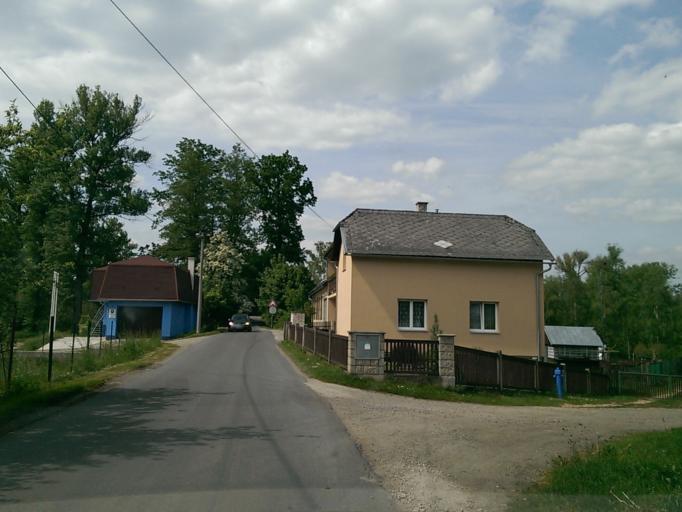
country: CZ
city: Prisovice
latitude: 50.5622
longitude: 15.0860
